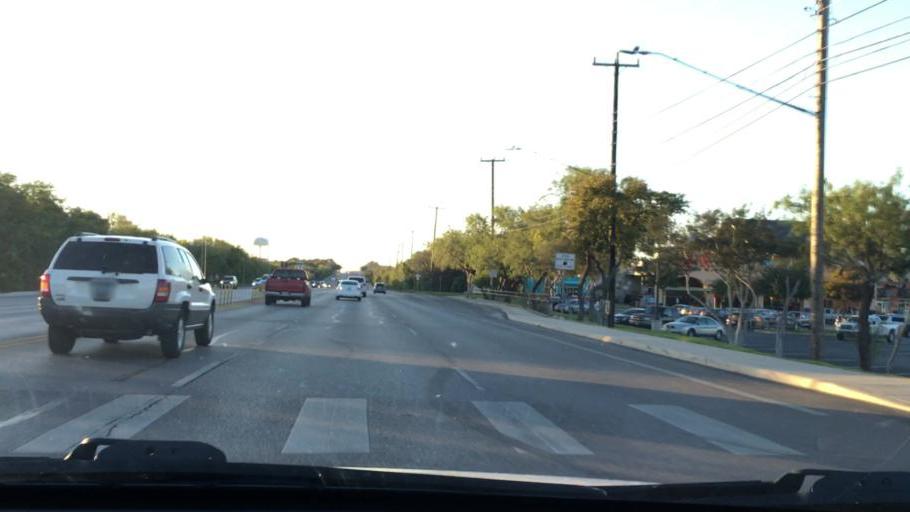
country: US
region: Texas
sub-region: Bexar County
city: Shavano Park
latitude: 29.5547
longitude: -98.5339
